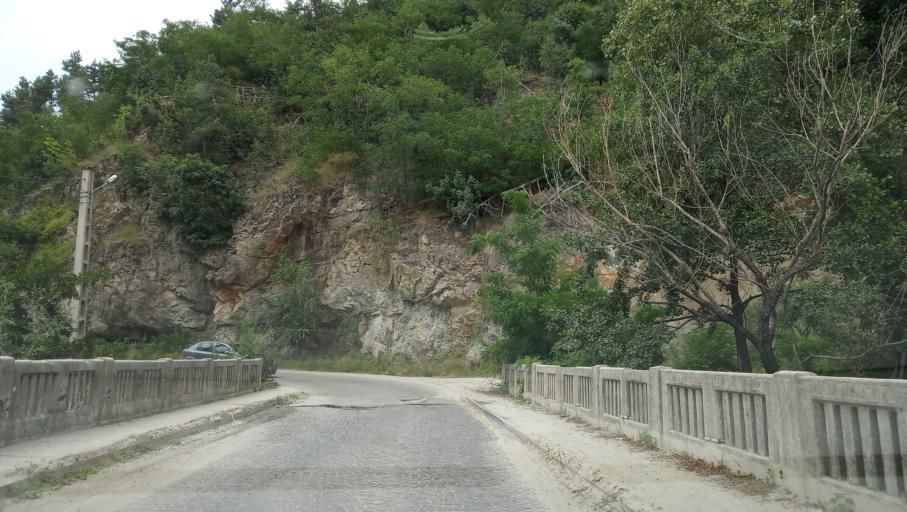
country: RO
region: Gorj
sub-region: Comuna Bumbesti-Jiu
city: Bumbesti-Jiu
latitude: 45.1802
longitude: 23.3726
